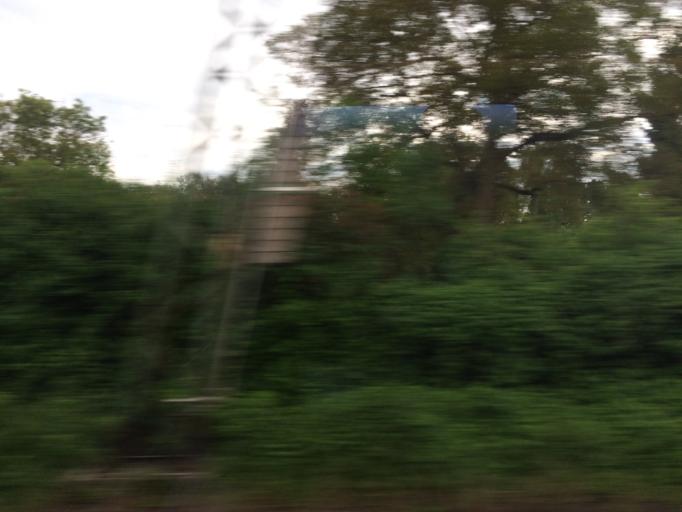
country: DE
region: Hesse
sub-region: Regierungsbezirk Darmstadt
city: Offenbach
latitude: 50.1389
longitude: 8.7791
